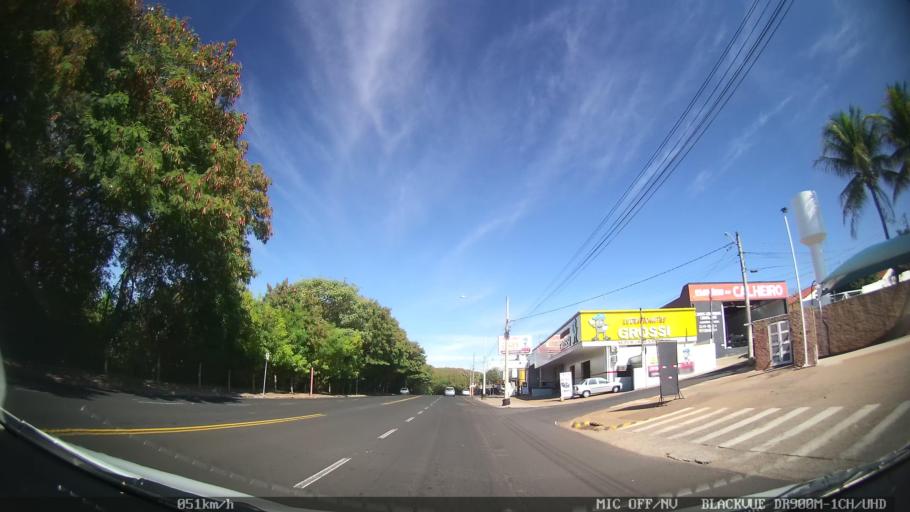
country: BR
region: Sao Paulo
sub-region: Sao Jose Do Rio Preto
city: Sao Jose do Rio Preto
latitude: -20.7997
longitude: -49.4032
